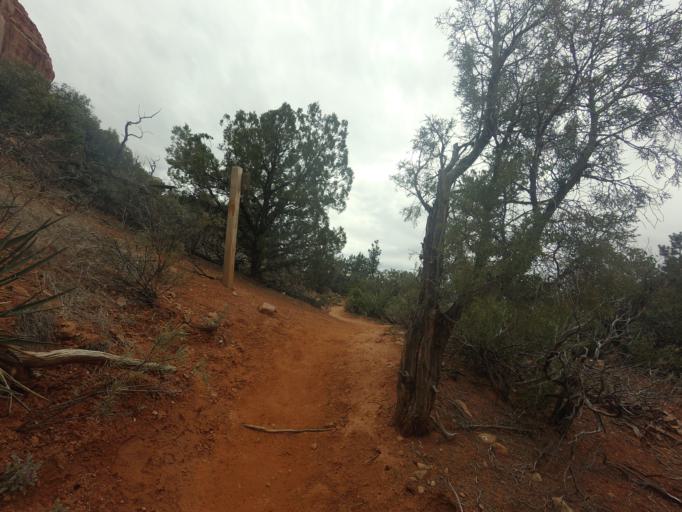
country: US
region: Arizona
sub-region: Yavapai County
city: Village of Oak Creek (Big Park)
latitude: 34.8015
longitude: -111.7609
